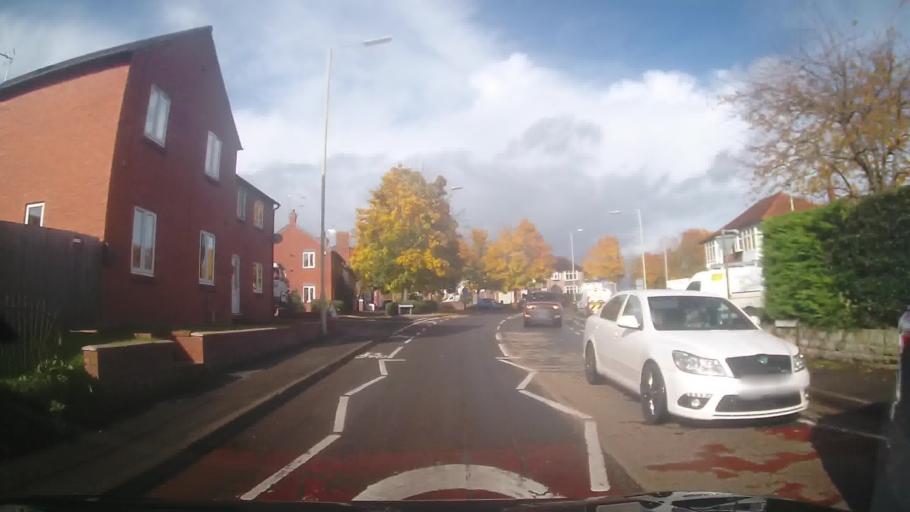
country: GB
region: England
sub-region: Shropshire
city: Whitchurch
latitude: 52.9638
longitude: -2.6793
